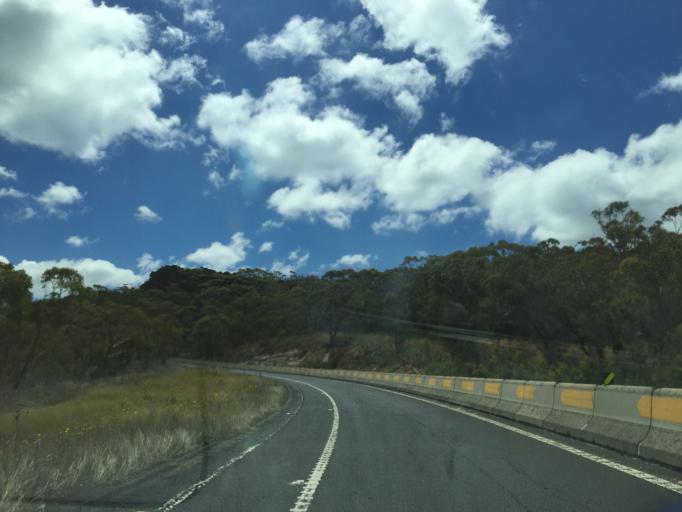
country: AU
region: New South Wales
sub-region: Blue Mountains Municipality
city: Blackheath
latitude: -33.5266
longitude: 150.3102
